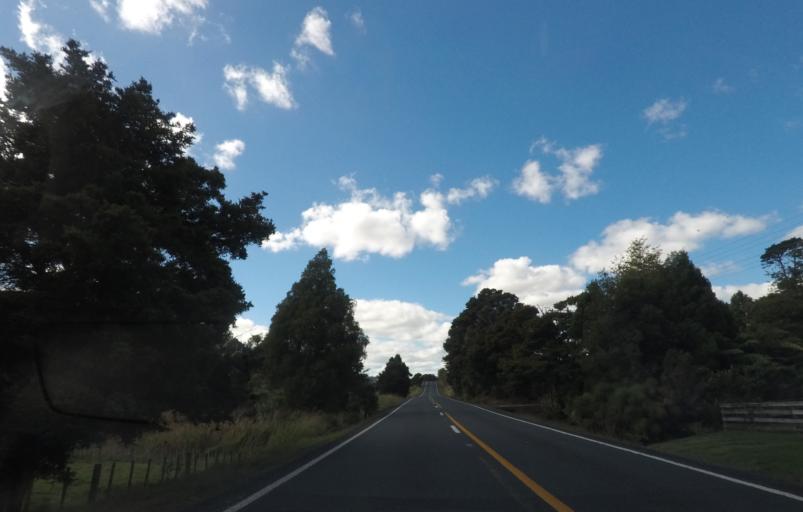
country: NZ
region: Auckland
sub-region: Auckland
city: Parakai
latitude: -36.6310
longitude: 174.5539
